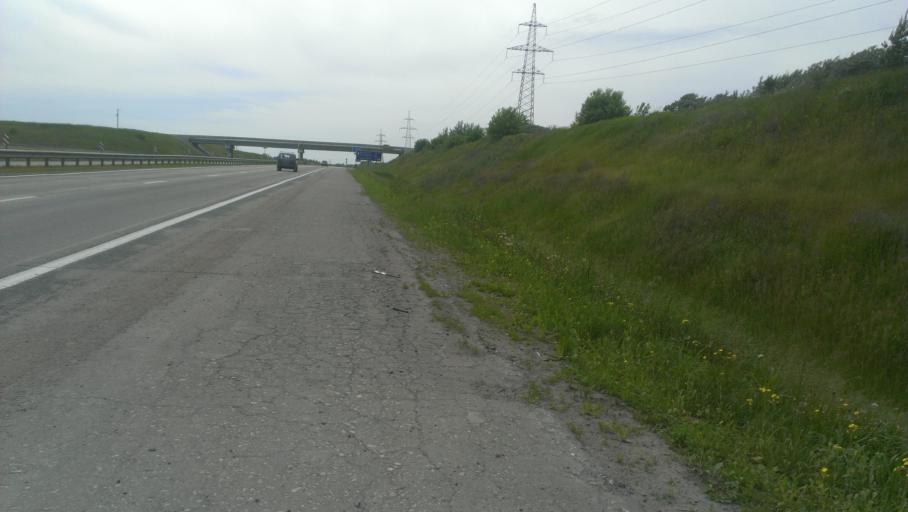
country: RU
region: Altai Krai
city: Sannikovo
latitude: 53.3426
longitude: 83.9388
